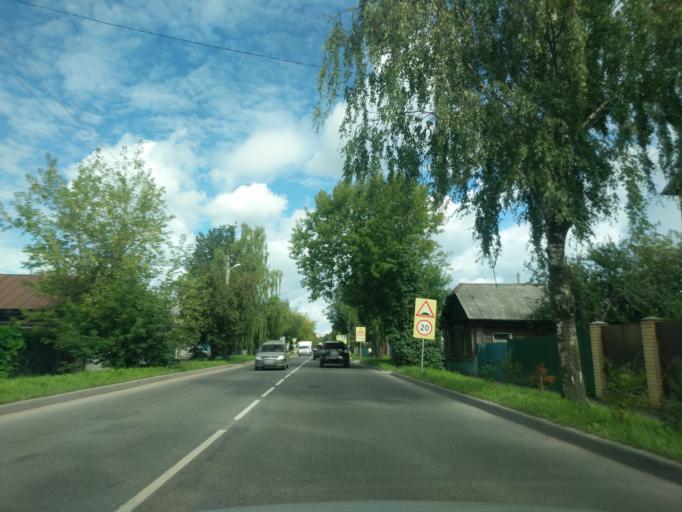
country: RU
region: Kostroma
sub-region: Kostromskoy Rayon
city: Kostroma
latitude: 57.7756
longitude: 40.9508
